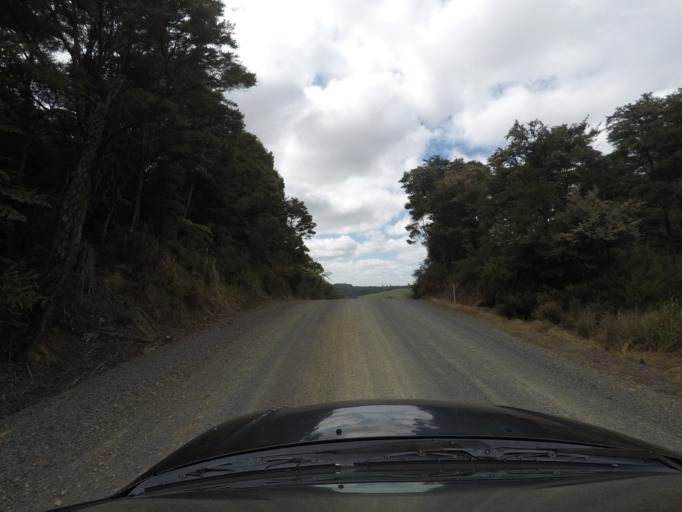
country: NZ
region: Northland
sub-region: Whangarei
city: Ruakaka
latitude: -35.9281
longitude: 174.3407
